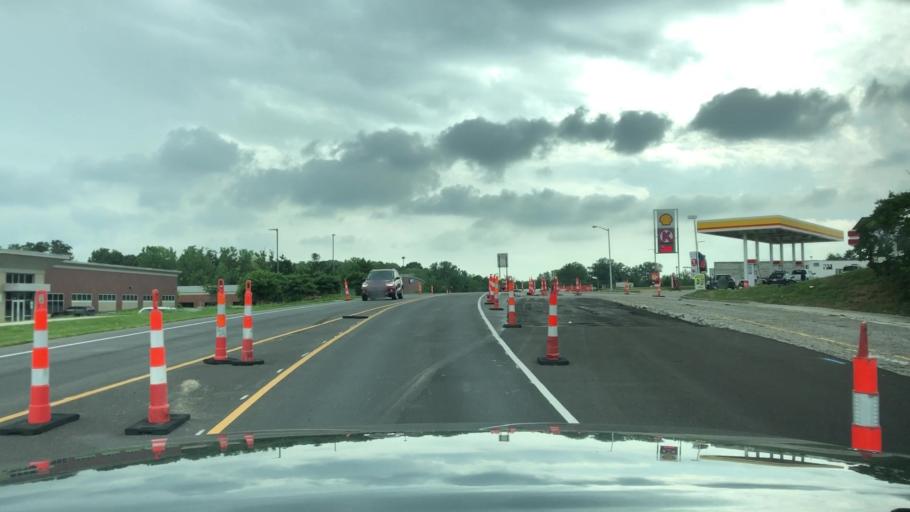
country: US
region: Missouri
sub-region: Saint Charles County
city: Saint Peters
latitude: 38.8048
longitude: -90.5533
